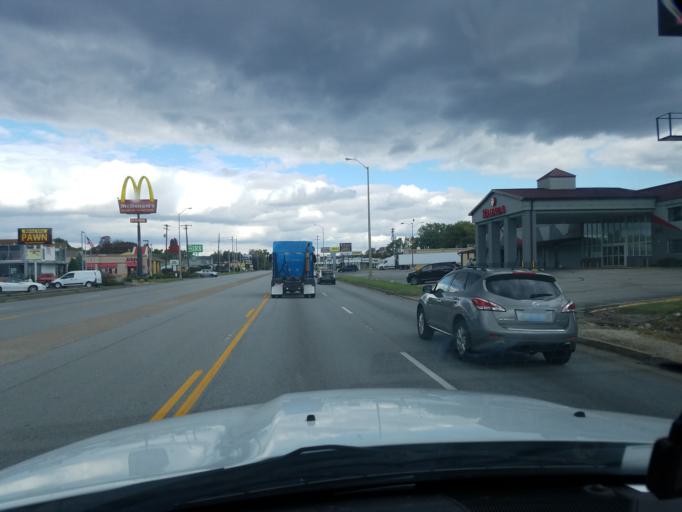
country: US
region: Kentucky
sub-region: Henderson County
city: Henderson
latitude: 37.8654
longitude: -87.5732
